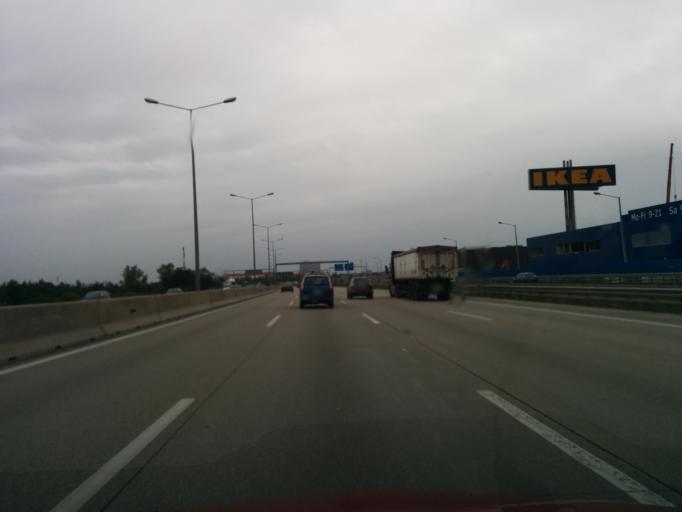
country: AT
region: Lower Austria
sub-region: Politischer Bezirk Modling
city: Vosendorf
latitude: 48.1068
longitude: 16.3201
